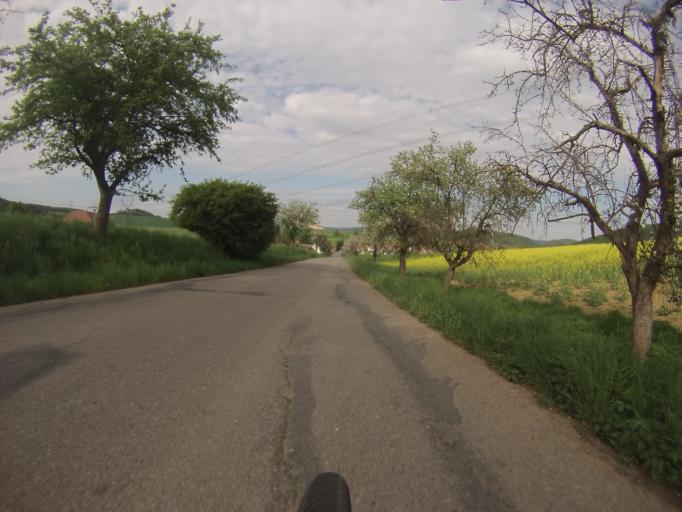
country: CZ
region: South Moravian
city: Veverska Bityska
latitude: 49.2916
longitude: 16.4503
